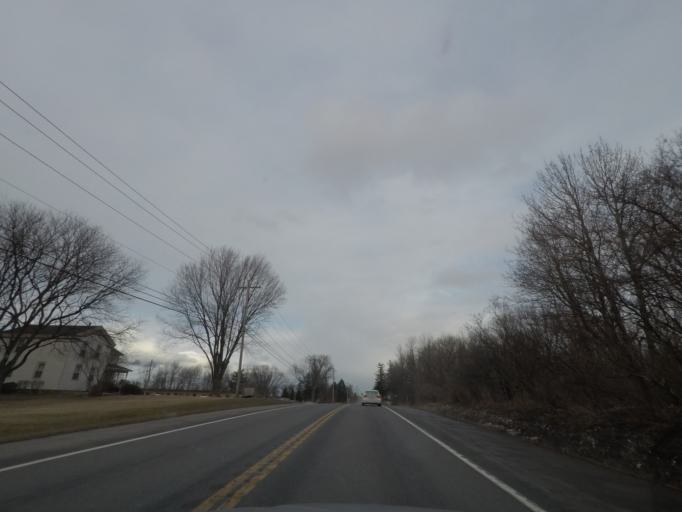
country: US
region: New York
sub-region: Oneida County
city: Vernon
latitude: 43.0734
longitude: -75.5079
